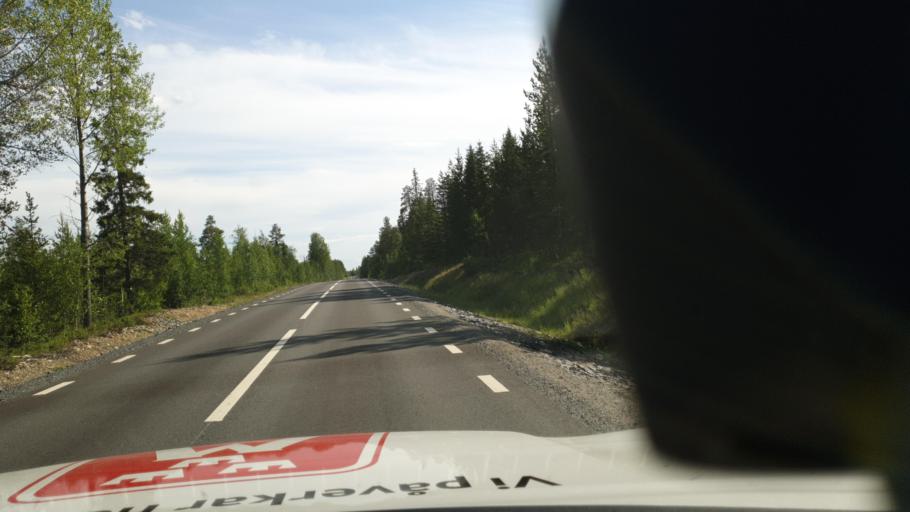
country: SE
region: Vaesterbotten
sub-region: Skelleftea Kommun
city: Langsele
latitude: 64.7668
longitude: 20.3406
